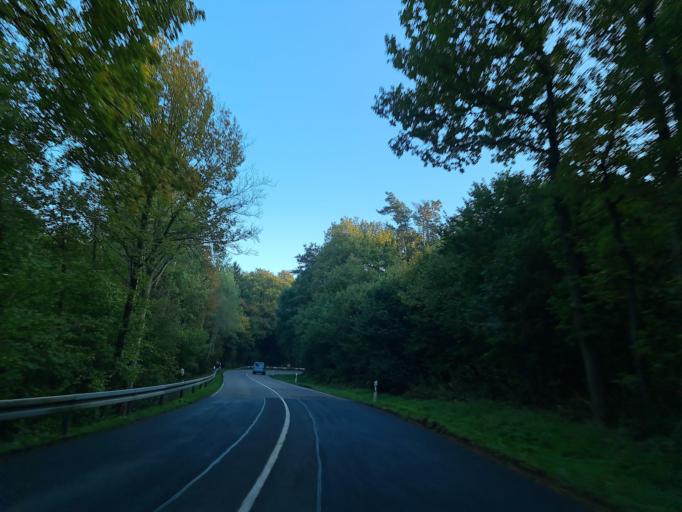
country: DE
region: Saxony
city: Elsterberg
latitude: 50.5781
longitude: 12.1292
